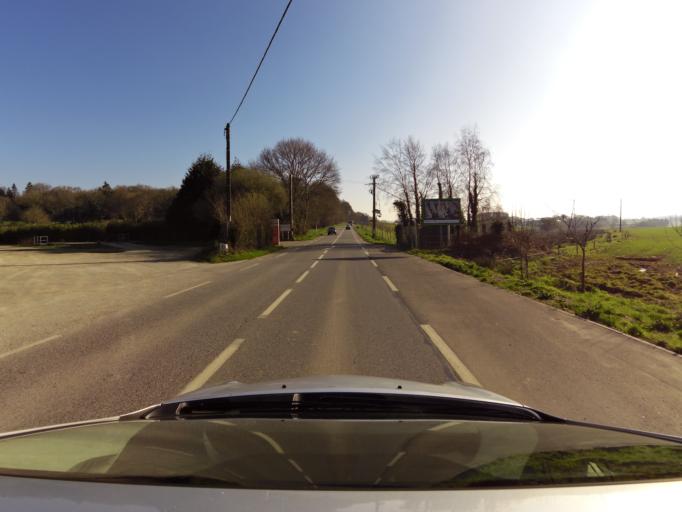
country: FR
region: Brittany
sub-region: Departement du Morbihan
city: Gestel
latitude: 47.8027
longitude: -3.4771
